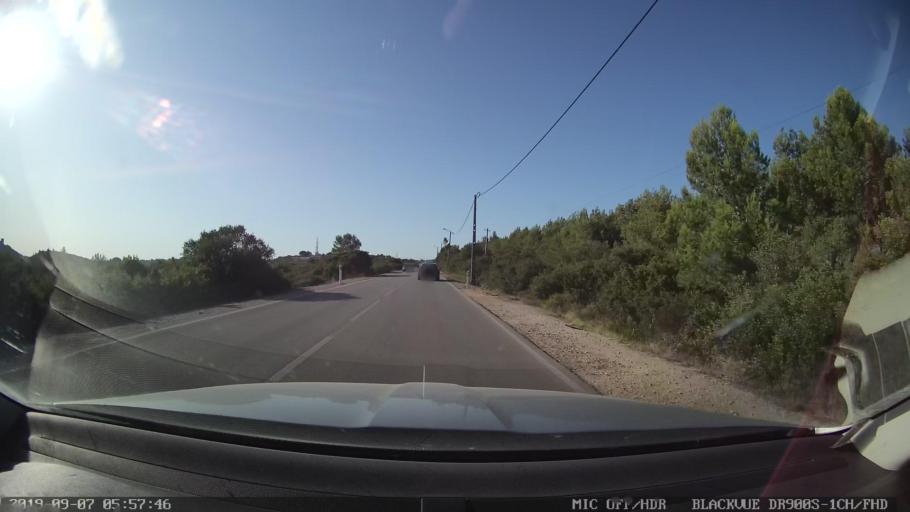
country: PT
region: Setubal
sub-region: Sesimbra
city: Sesimbra
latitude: 38.4539
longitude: -9.0913
